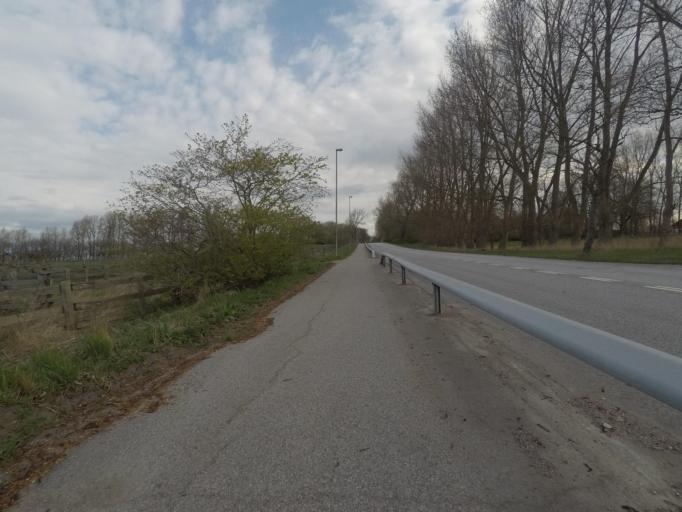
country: SE
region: Skane
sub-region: Lomma Kommun
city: Lomma
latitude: 55.6533
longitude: 13.0550
